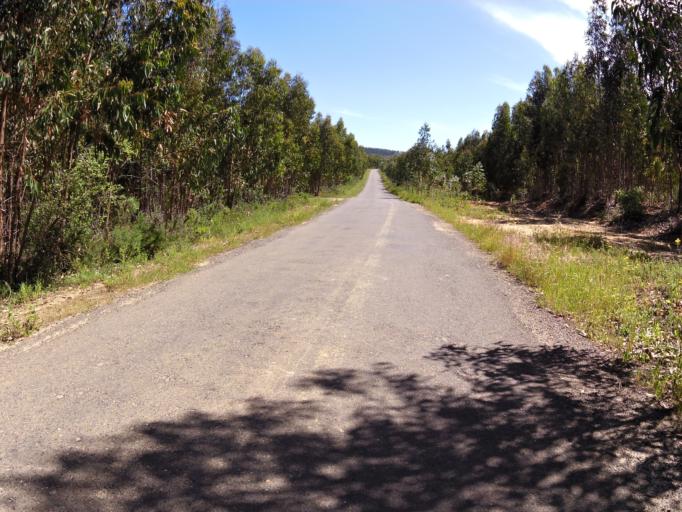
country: PT
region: Setubal
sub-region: Santiago do Cacem
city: Santiago do Cacem
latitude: 37.9457
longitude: -8.7278
